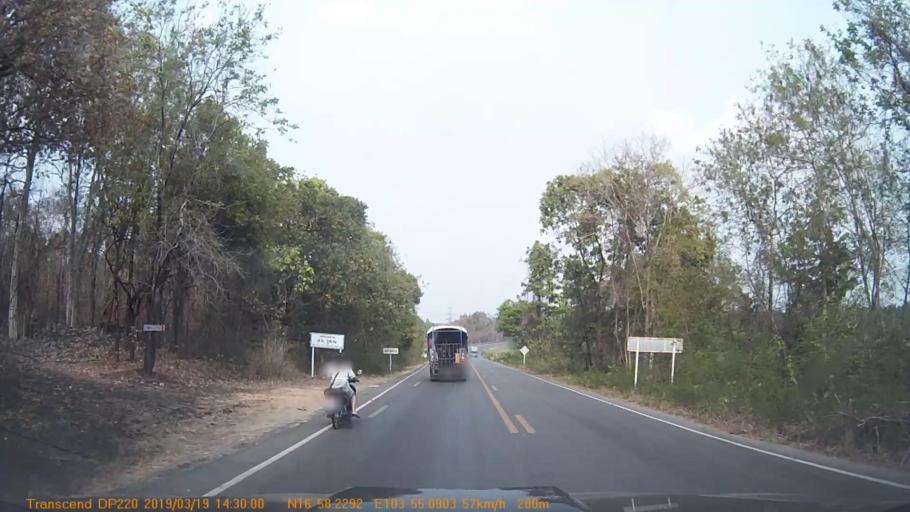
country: TH
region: Sakon Nakhon
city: Phu Phan
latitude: 16.9707
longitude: 103.9186
